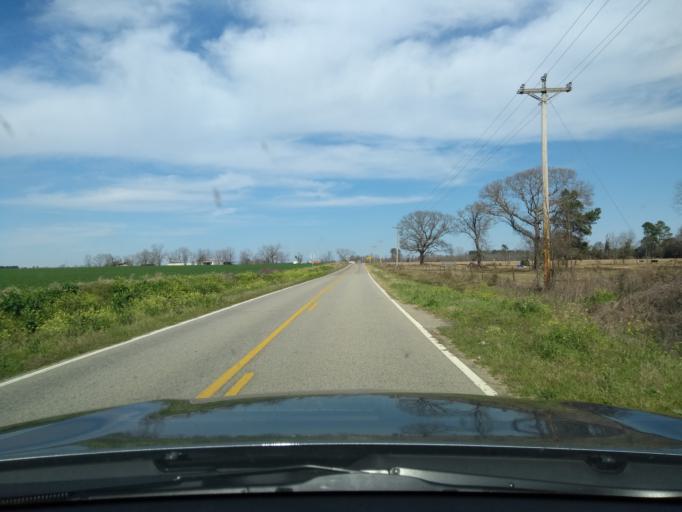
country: US
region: Georgia
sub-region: Bulloch County
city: Brooklet
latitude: 32.4552
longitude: -81.6613
